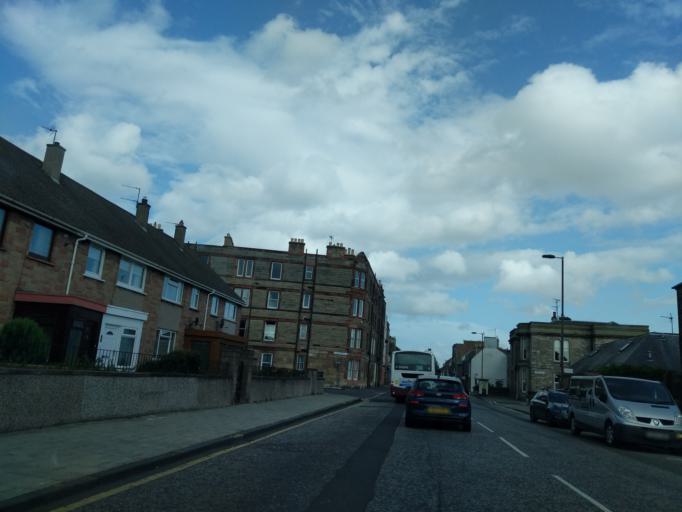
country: GB
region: Scotland
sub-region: East Lothian
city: Musselburgh
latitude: 55.9440
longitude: -3.0639
